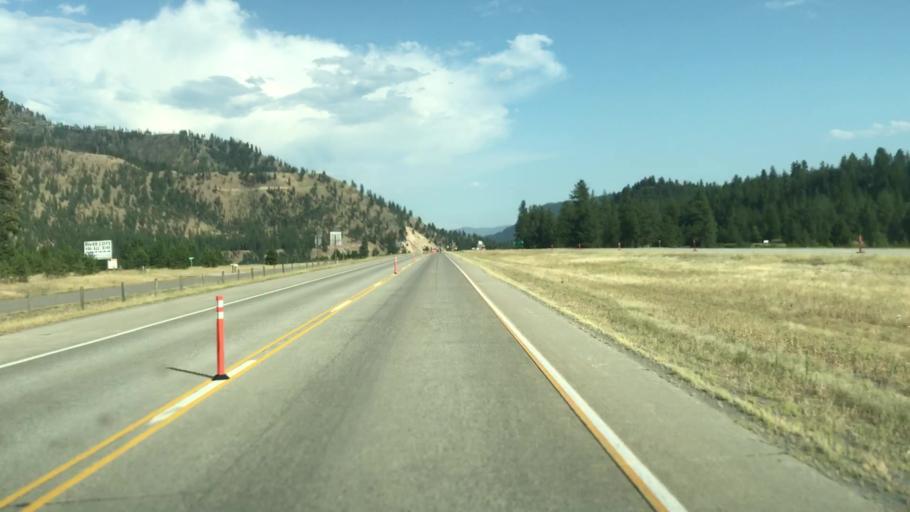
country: US
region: Montana
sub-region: Mineral County
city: Superior
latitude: 47.2310
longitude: -114.9801
